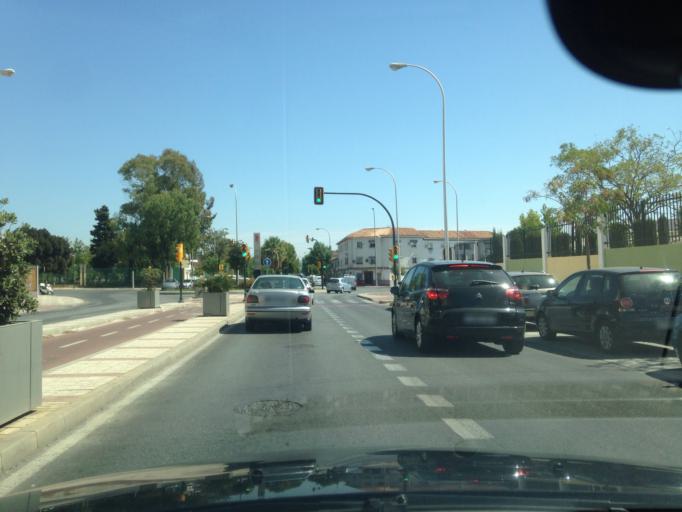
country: ES
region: Andalusia
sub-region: Provincia de Malaga
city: Malaga
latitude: 36.7191
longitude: -4.4501
